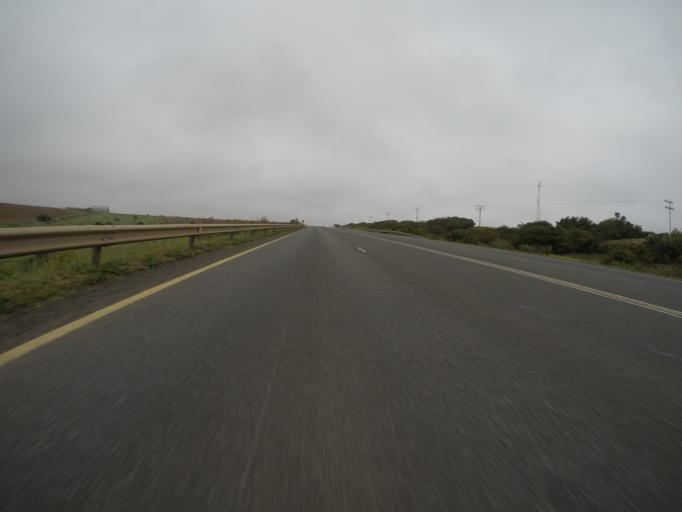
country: ZA
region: Western Cape
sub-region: Eden District Municipality
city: Riversdale
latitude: -34.1499
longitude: 21.2956
